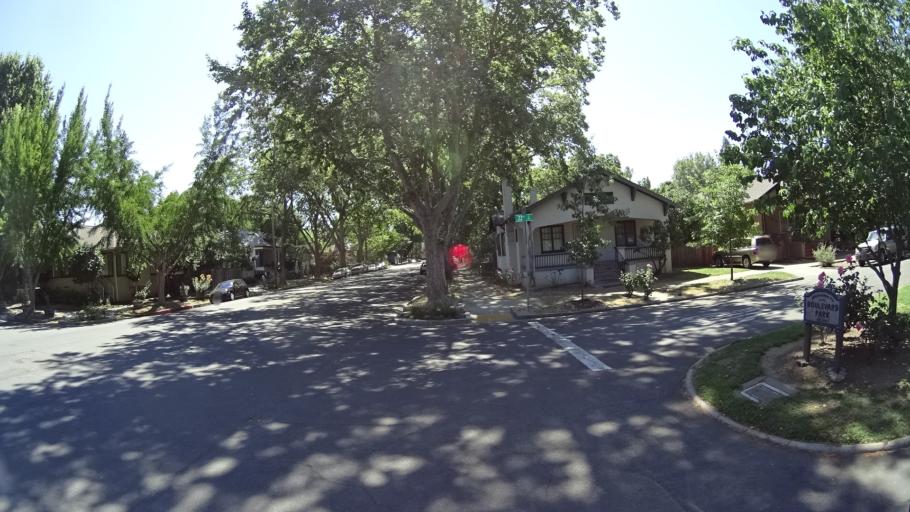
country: US
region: California
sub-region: Sacramento County
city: Sacramento
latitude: 38.5836
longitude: -121.4740
